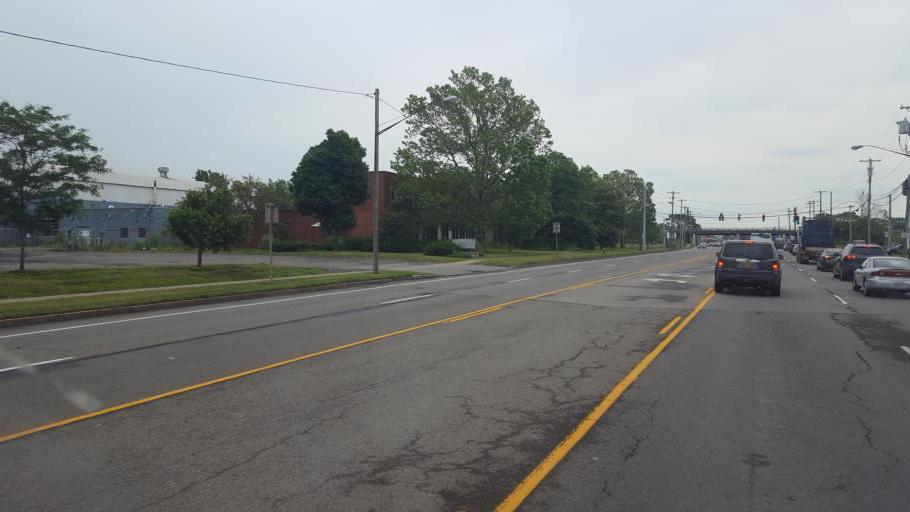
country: US
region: New York
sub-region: Niagara County
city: Niagara Falls
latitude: 43.0900
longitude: -78.9940
